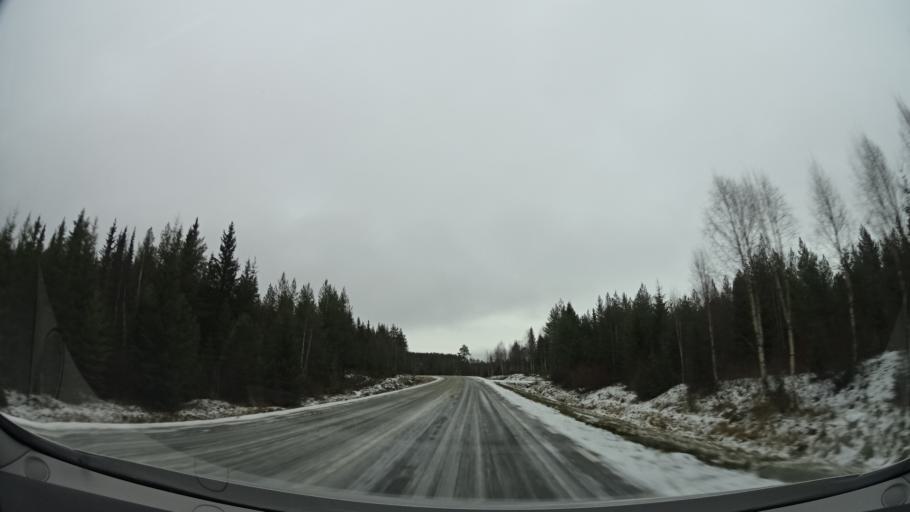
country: SE
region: Vaesterbotten
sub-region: Lycksele Kommun
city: Lycksele
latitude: 64.5142
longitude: 18.3773
